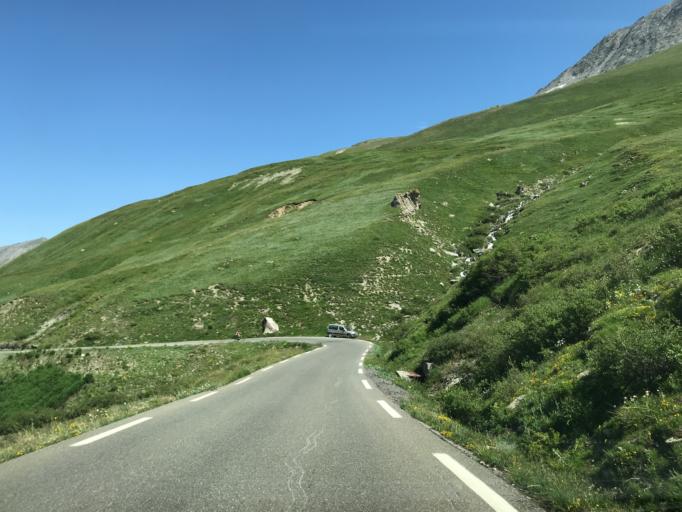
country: IT
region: Piedmont
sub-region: Provincia di Cuneo
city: Pontechianale
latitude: 44.6986
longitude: 6.9462
